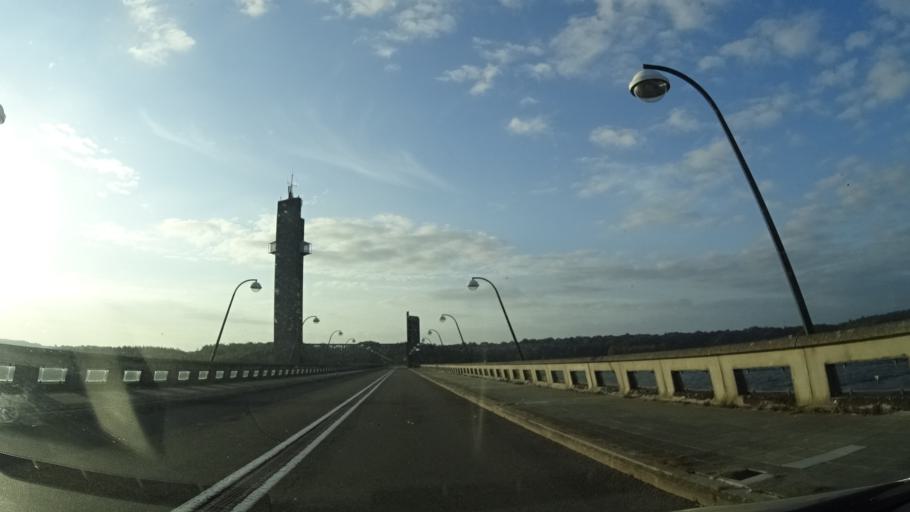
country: BE
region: Wallonia
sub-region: Province de Namur
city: Cerfontaine
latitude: 50.1905
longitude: 4.3845
